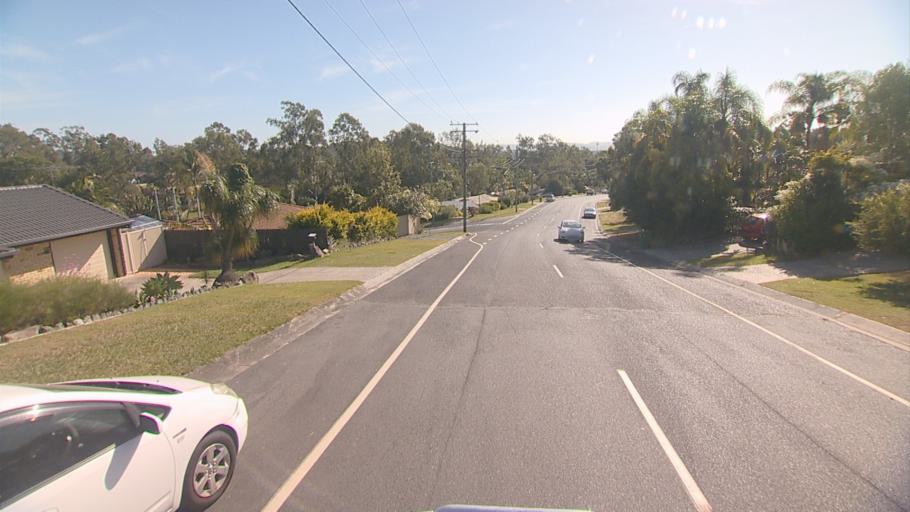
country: AU
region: Queensland
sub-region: Logan
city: Windaroo
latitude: -27.7220
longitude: 153.1813
